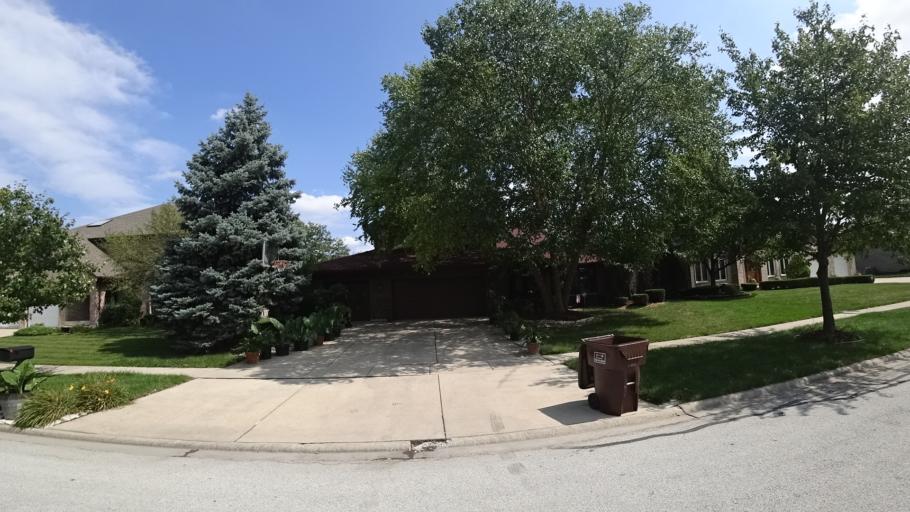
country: US
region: Illinois
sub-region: Cook County
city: Tinley Park
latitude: 41.5685
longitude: -87.8134
